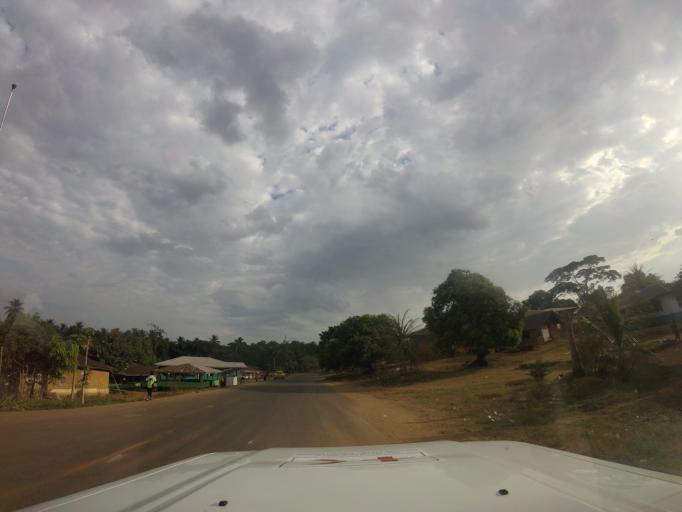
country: LR
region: Grand Cape Mount
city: Robertsport
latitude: 6.7645
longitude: -11.1496
